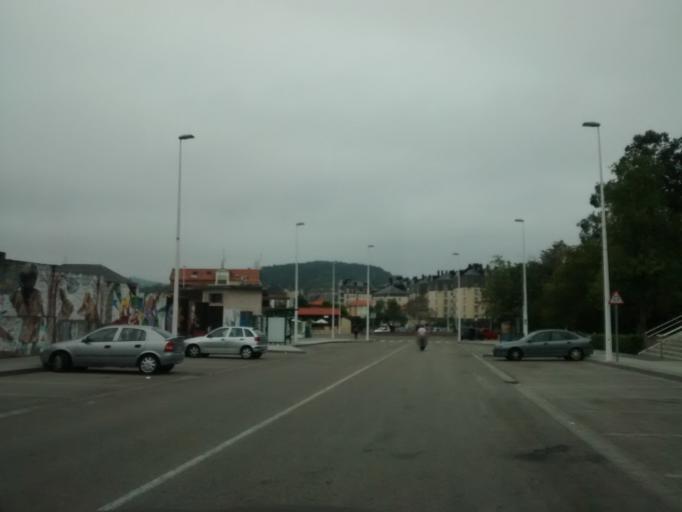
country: ES
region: Cantabria
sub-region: Provincia de Cantabria
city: Torrelavega
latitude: 43.3443
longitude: -4.0515
